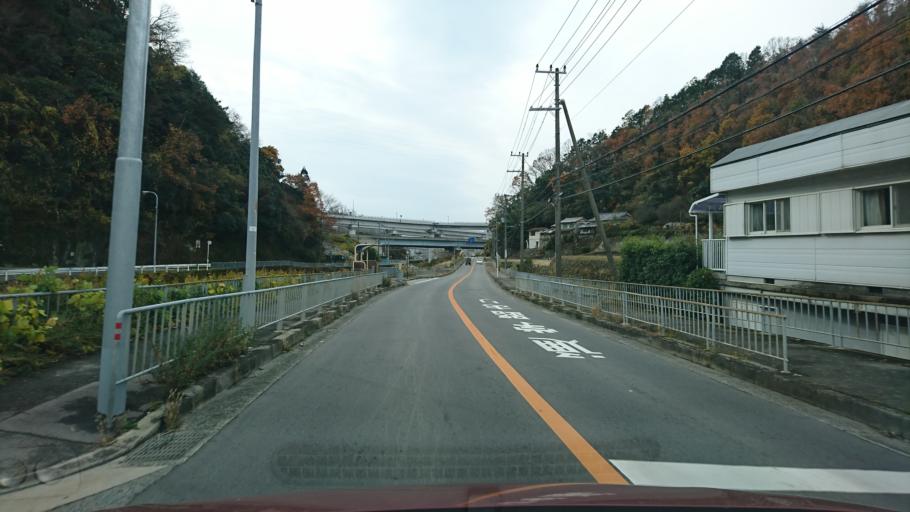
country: JP
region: Osaka
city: Mino
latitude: 34.8792
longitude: 135.4589
